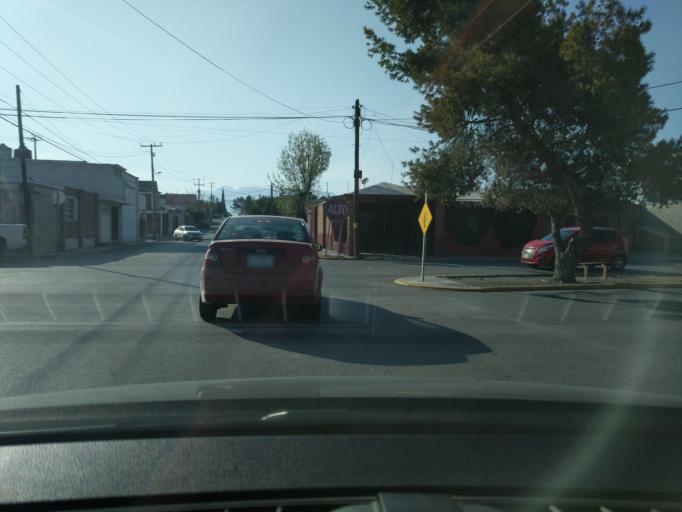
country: MX
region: Coahuila
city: Saltillo
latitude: 25.4635
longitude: -100.9870
